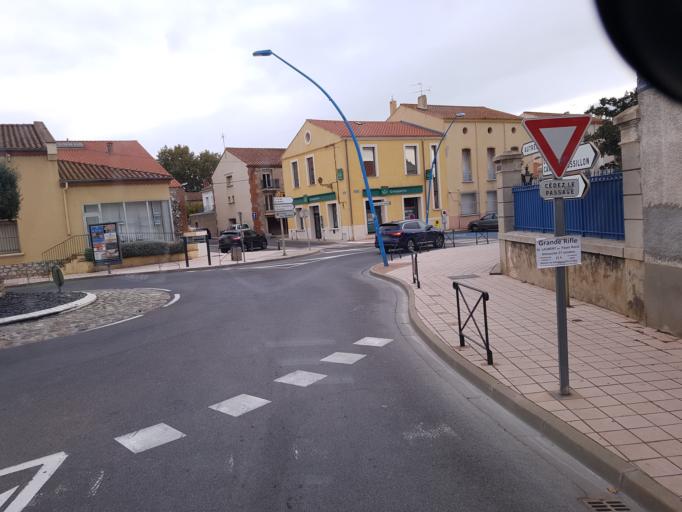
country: FR
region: Languedoc-Roussillon
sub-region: Departement des Pyrenees-Orientales
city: Saint-Laurent-de-la-Salanque
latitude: 42.7730
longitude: 2.9876
